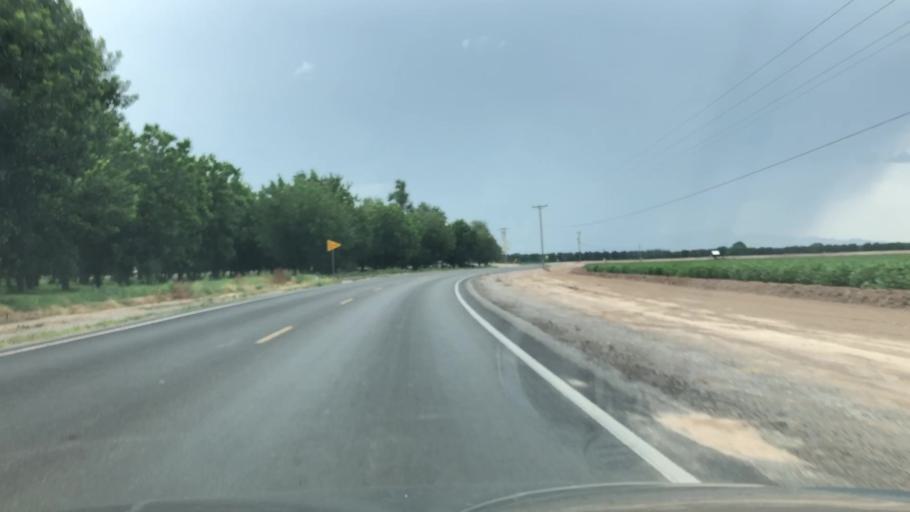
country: US
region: New Mexico
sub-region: Dona Ana County
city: La Union
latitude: 31.9719
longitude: -106.6519
